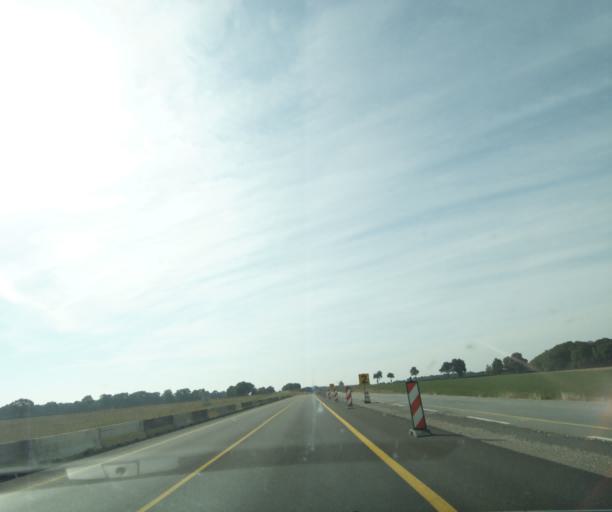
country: FR
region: Bourgogne
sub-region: Departement de Saone-et-Loire
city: Paray-le-Monial
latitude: 46.5095
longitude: 4.1620
